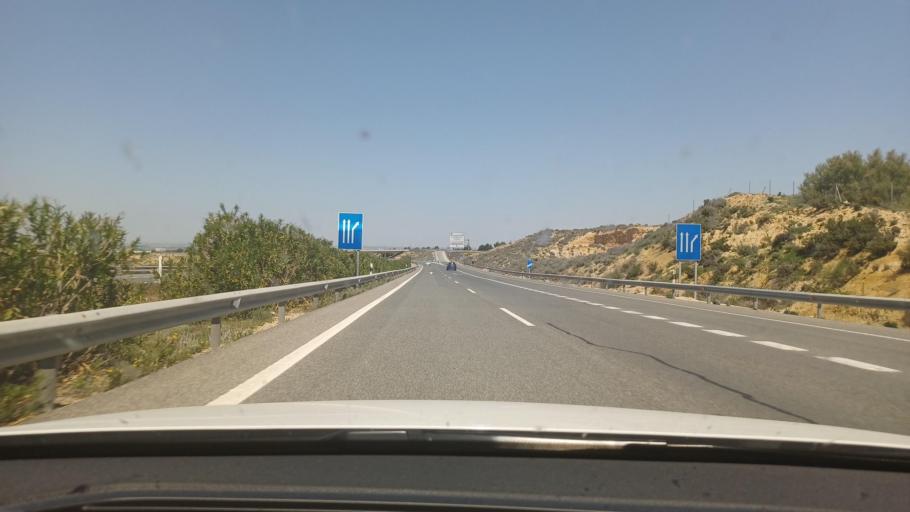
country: ES
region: Castille-La Mancha
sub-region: Provincia de Albacete
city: Chinchilla de Monte Aragon
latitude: 38.9238
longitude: -1.7366
